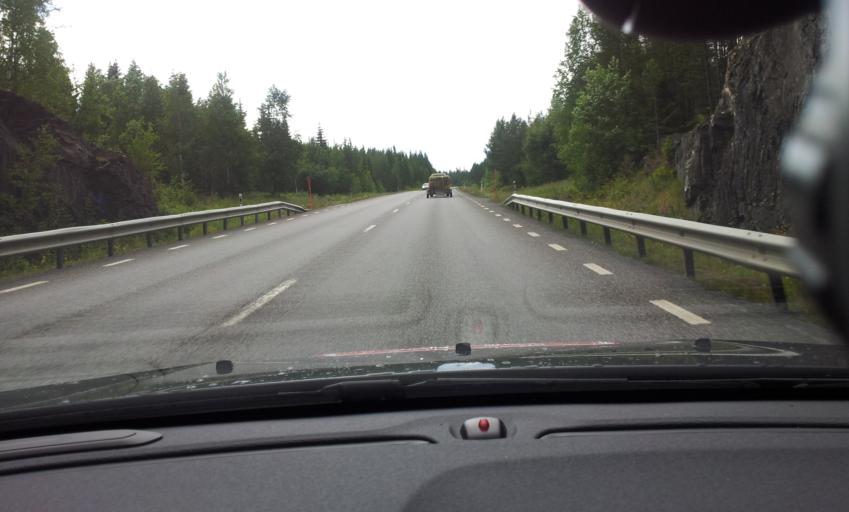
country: SE
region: Jaemtland
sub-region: Krokoms Kommun
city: Valla
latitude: 63.3125
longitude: 13.7359
